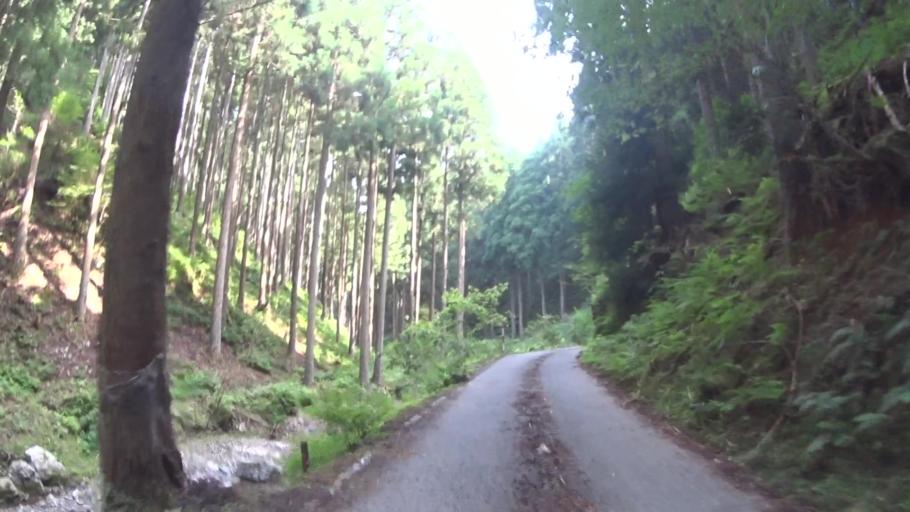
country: JP
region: Fukui
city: Obama
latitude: 35.2689
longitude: 135.6429
